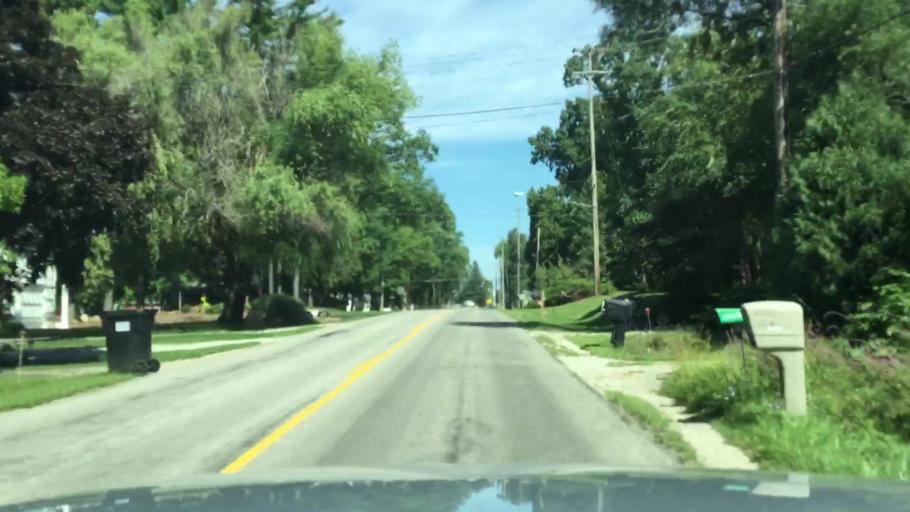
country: US
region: Michigan
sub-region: Lenawee County
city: Manitou Beach-Devils Lake
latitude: 42.0005
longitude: -84.2808
